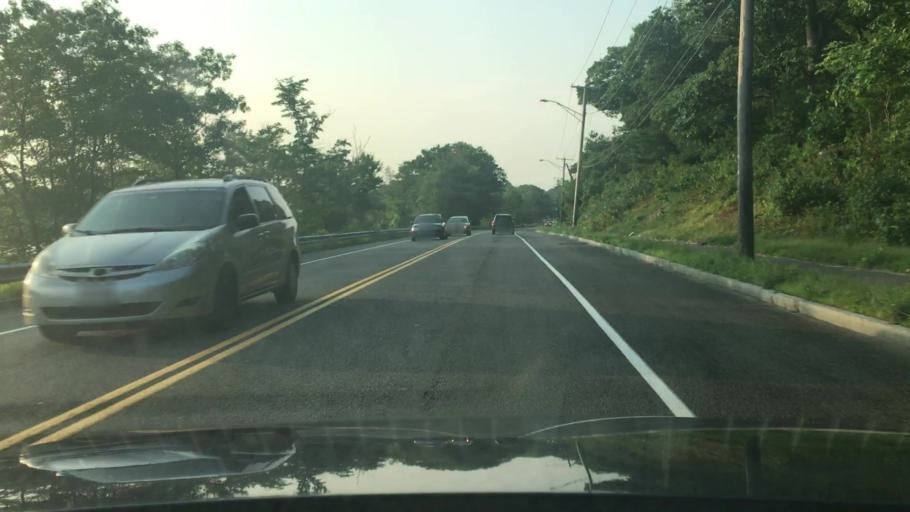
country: US
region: Massachusetts
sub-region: Essex County
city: Saugus
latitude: 42.4796
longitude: -71.0057
